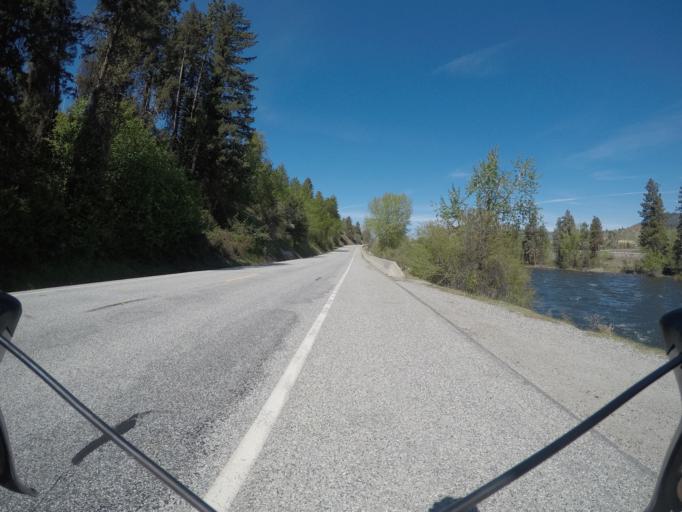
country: US
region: Washington
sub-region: Chelan County
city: Cashmere
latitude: 47.5331
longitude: -120.5492
